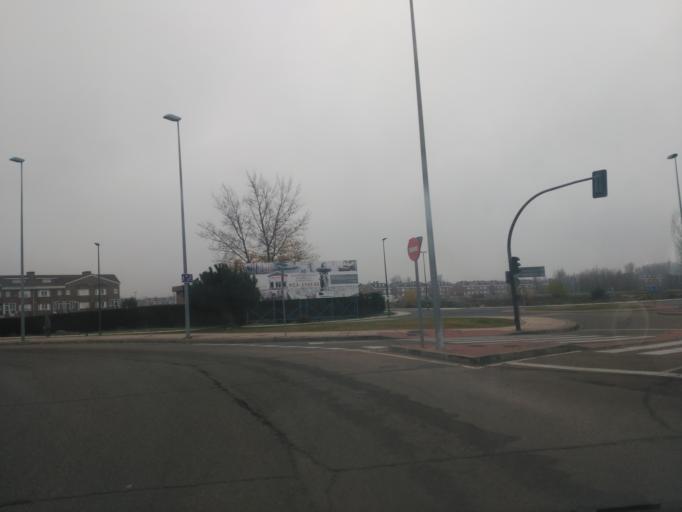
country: ES
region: Castille and Leon
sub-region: Provincia de Salamanca
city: Santa Marta de Tormes
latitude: 40.9578
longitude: -5.6456
